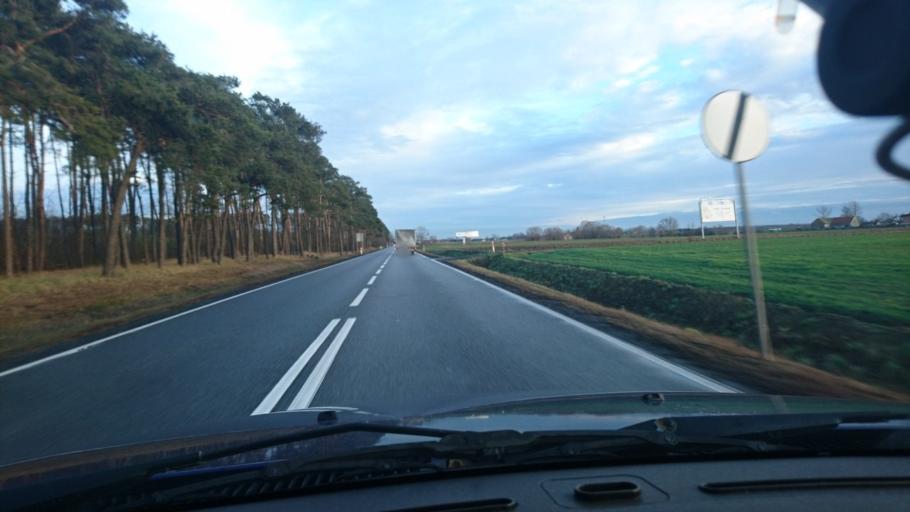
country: PL
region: Greater Poland Voivodeship
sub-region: Powiat kepinski
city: Leka Opatowska
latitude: 51.2227
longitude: 18.1206
